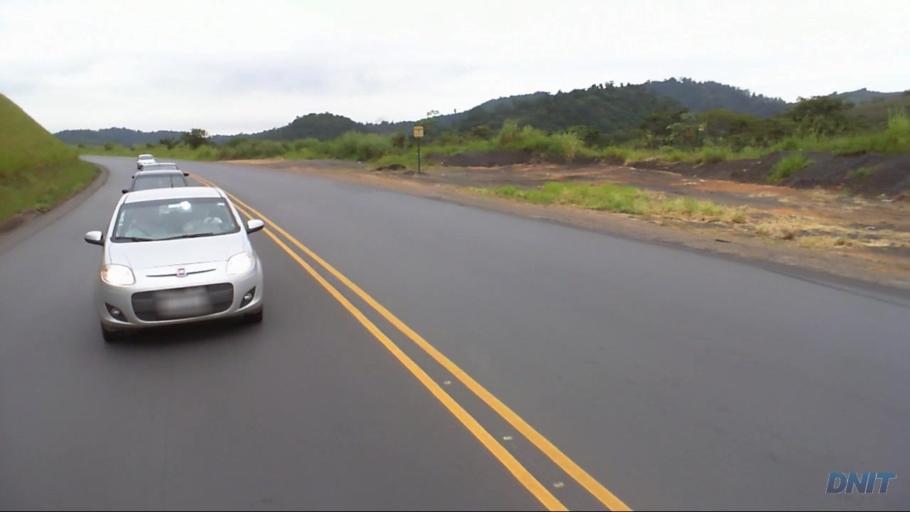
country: BR
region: Minas Gerais
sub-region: Coronel Fabriciano
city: Coronel Fabriciano
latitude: -19.5353
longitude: -42.5931
